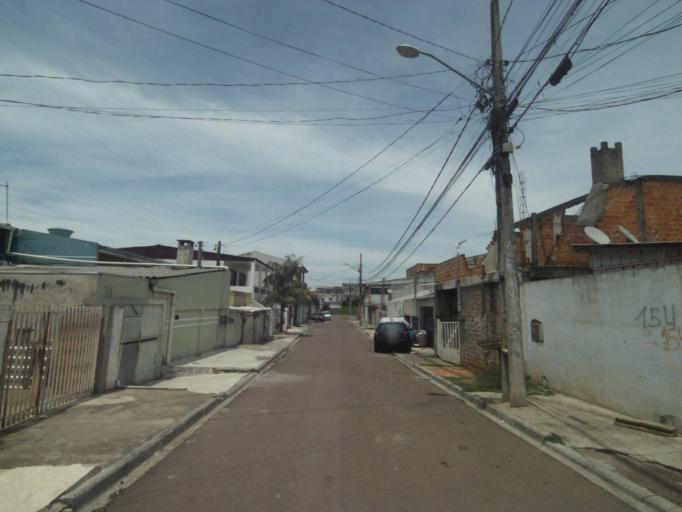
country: BR
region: Parana
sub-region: Curitiba
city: Curitiba
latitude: -25.5015
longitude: -49.3402
